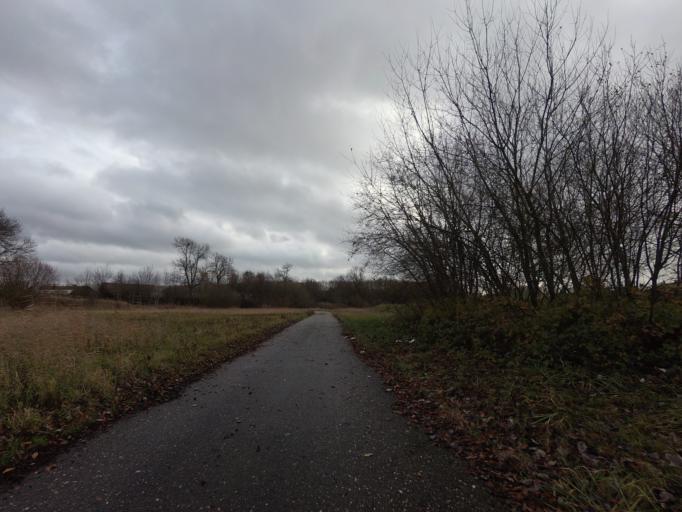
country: NL
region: North Brabant
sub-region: Gemeente Woensdrecht
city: Woensdrecht
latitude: 51.3783
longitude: 4.3056
